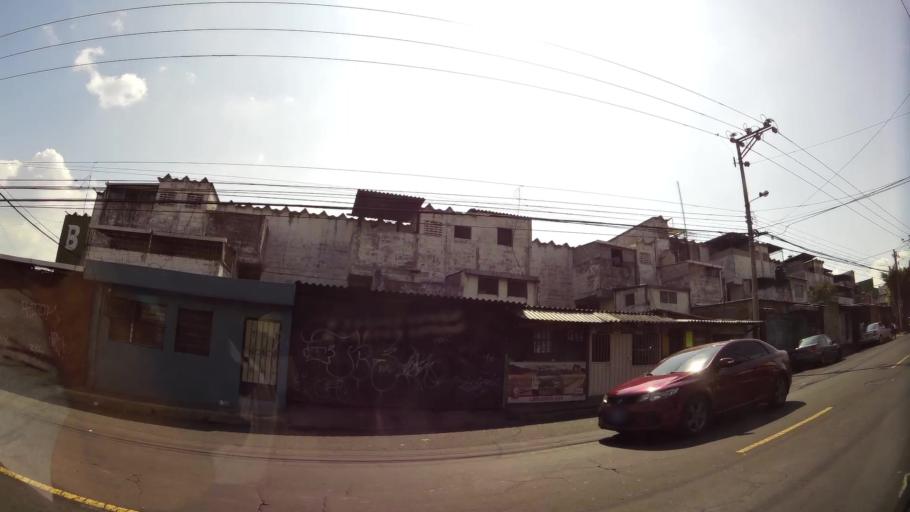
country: SV
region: San Salvador
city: Mejicanos
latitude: 13.7232
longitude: -89.2213
